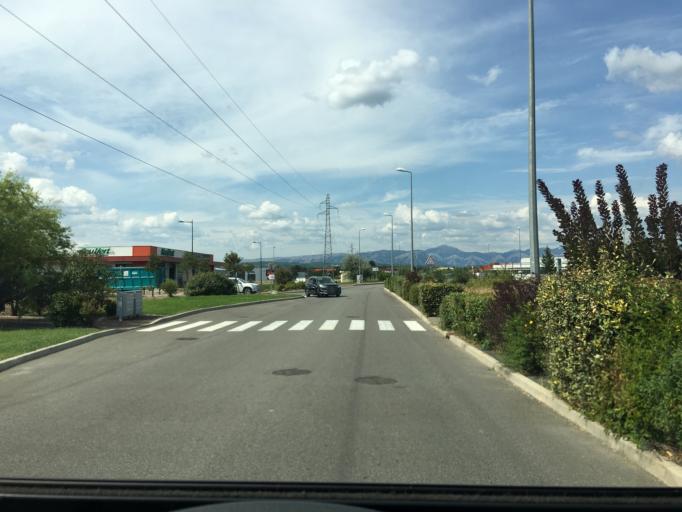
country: FR
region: Provence-Alpes-Cote d'Azur
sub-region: Departement des Alpes-de-Haute-Provence
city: Sisteron
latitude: 44.2350
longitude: 5.9111
